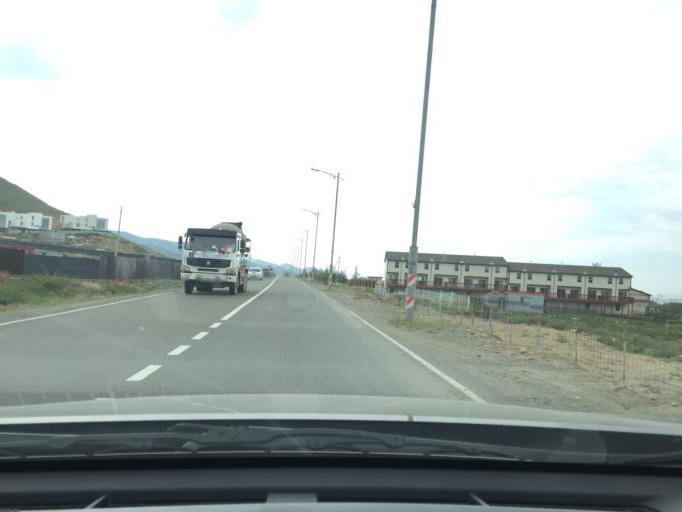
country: MN
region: Ulaanbaatar
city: Ulaanbaatar
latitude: 47.8864
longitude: 107.0067
